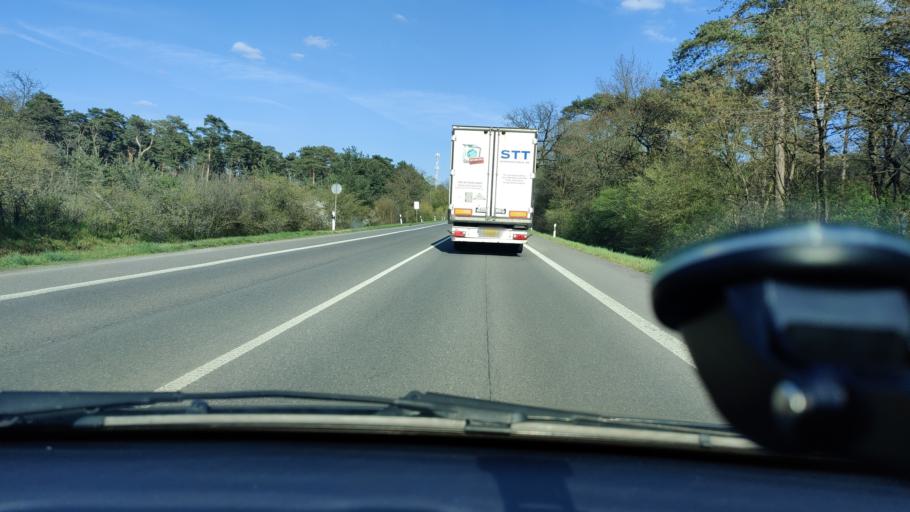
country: DE
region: North Rhine-Westphalia
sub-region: Regierungsbezirk Dusseldorf
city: Schermbeck
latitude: 51.7005
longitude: 6.9204
